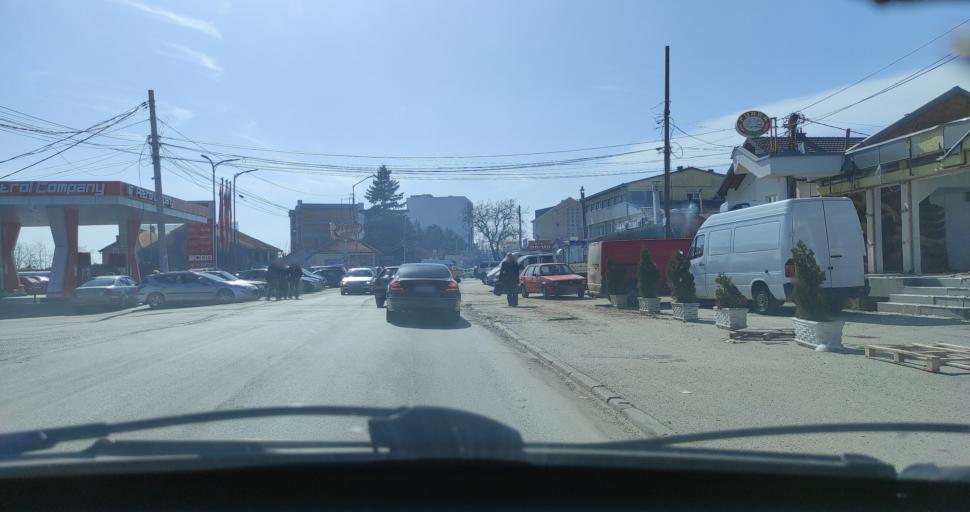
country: XK
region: Gjakova
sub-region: Komuna e Decanit
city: Decan
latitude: 42.5443
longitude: 20.2902
